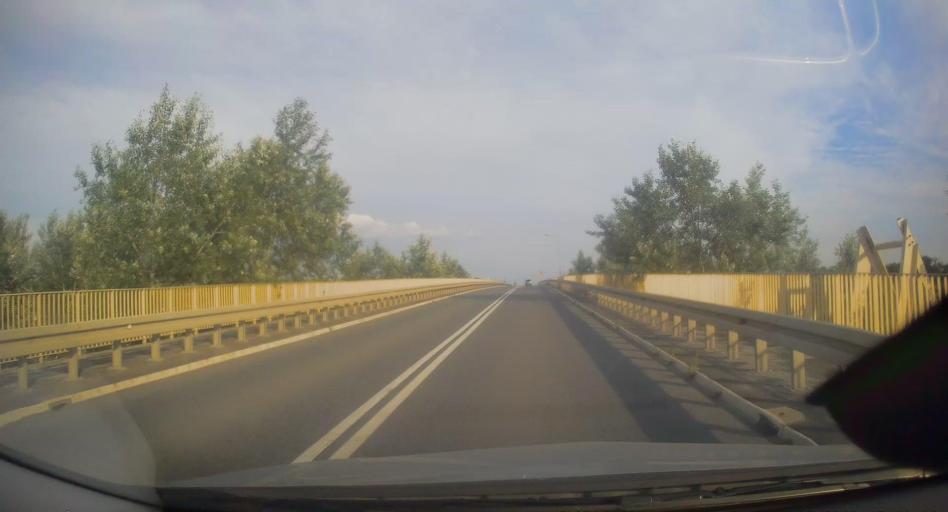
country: PL
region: Lesser Poland Voivodeship
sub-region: Powiat brzeski
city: Szczurowa
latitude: 50.1547
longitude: 20.6078
